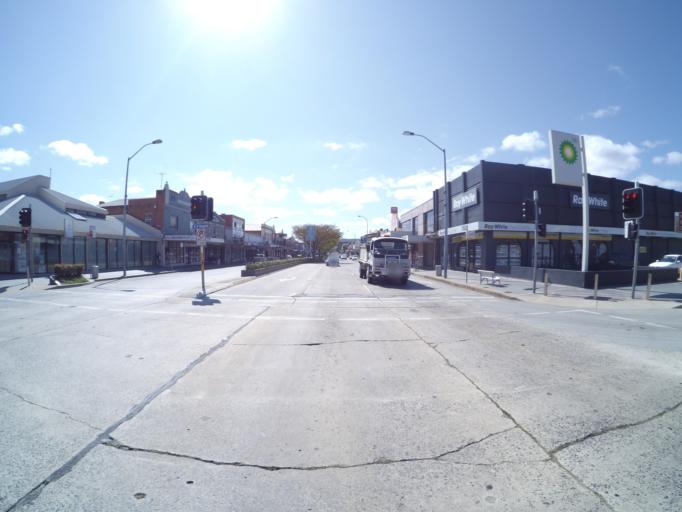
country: AU
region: New South Wales
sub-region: Queanbeyan
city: Queanbeyan
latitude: -35.3544
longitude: 149.2323
